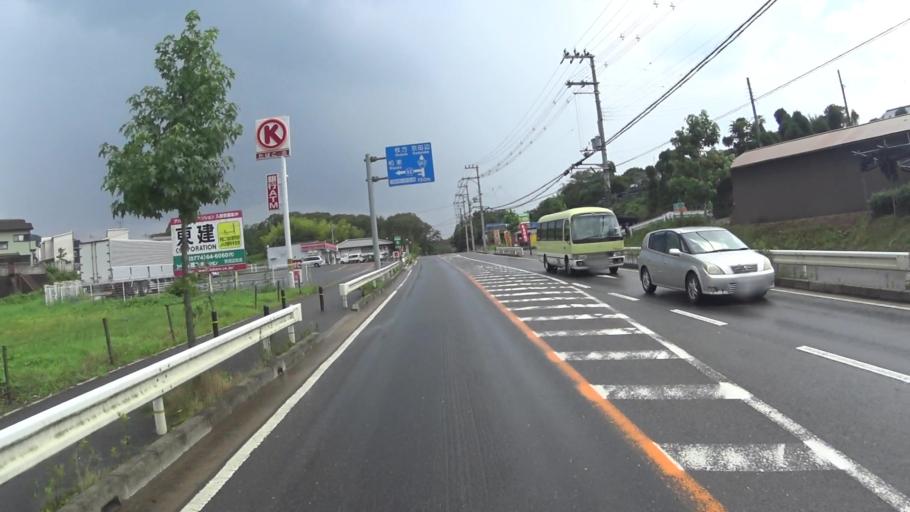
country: JP
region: Kyoto
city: Uji
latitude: 34.8461
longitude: 135.8435
